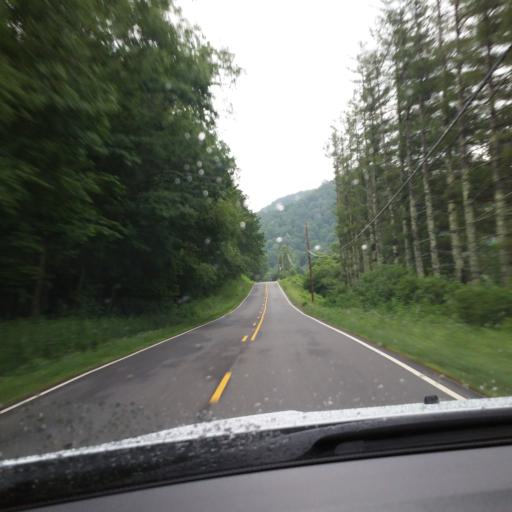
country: US
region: North Carolina
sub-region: Yancey County
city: Burnsville
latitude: 35.7761
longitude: -82.1996
